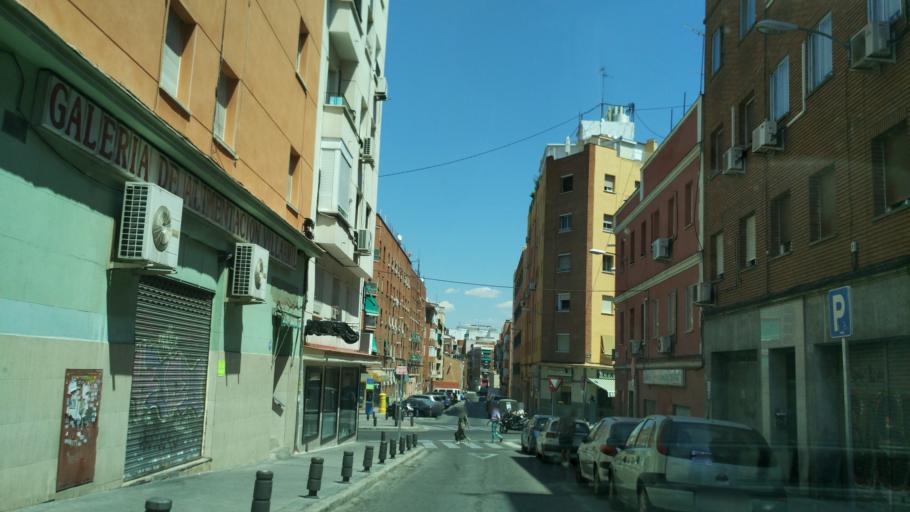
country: ES
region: Madrid
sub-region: Provincia de Madrid
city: Tetuan de las Victorias
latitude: 40.4587
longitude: -3.7075
